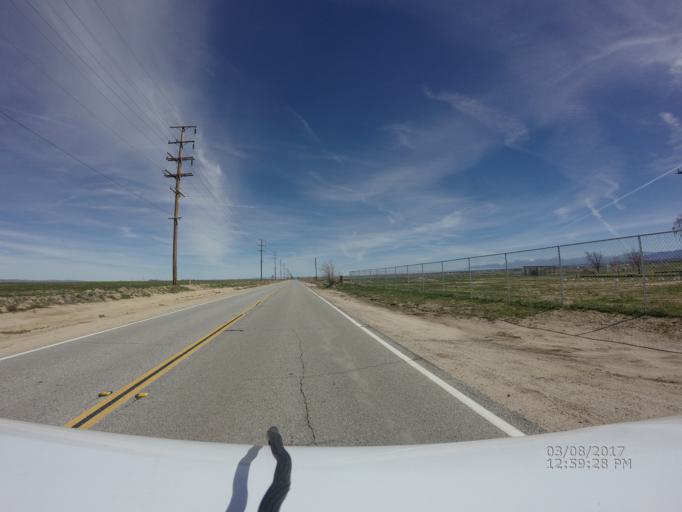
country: US
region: California
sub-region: Los Angeles County
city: Quartz Hill
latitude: 34.7187
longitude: -118.2538
